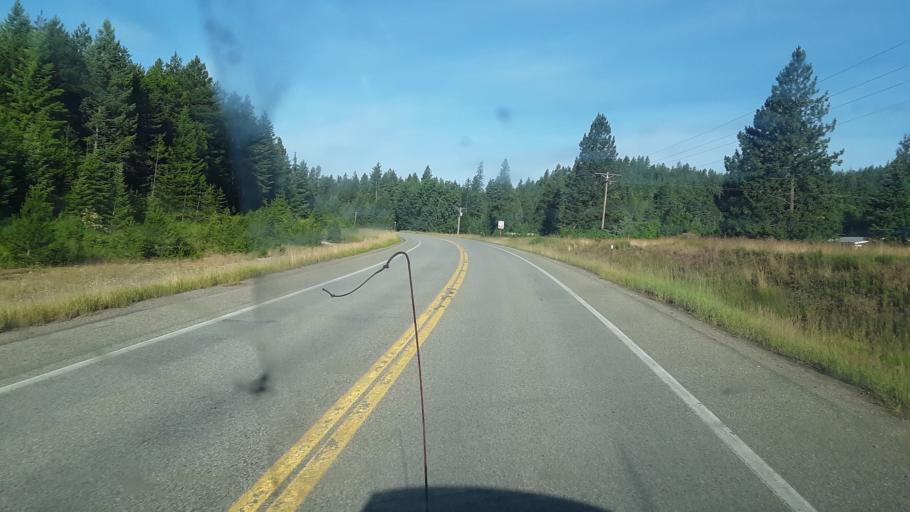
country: US
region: Idaho
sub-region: Boundary County
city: Bonners Ferry
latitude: 48.7325
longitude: -116.1873
